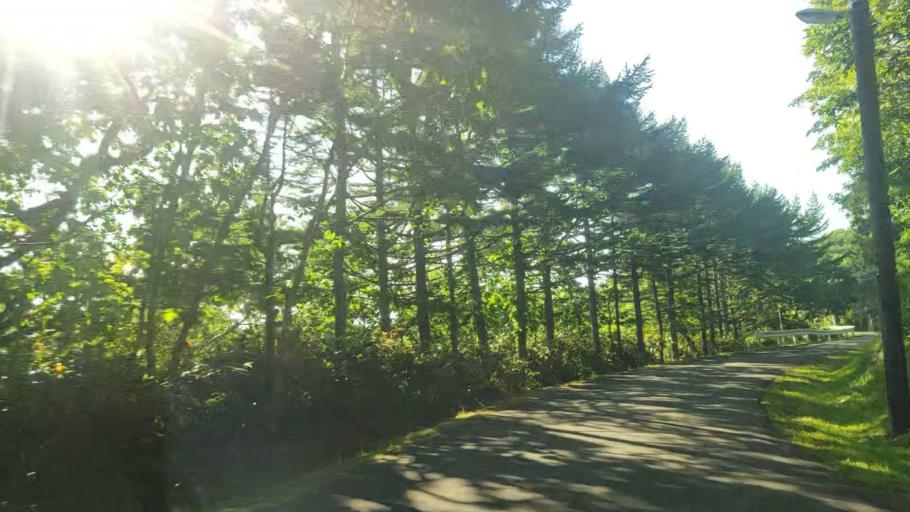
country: JP
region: Hokkaido
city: Wakkanai
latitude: 45.4140
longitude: 141.6685
